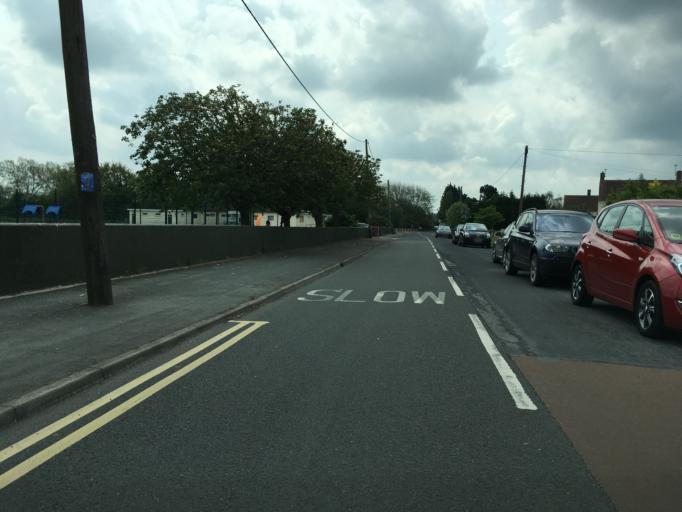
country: GB
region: England
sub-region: South Gloucestershire
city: Severn Beach
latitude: 51.5600
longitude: -2.6626
